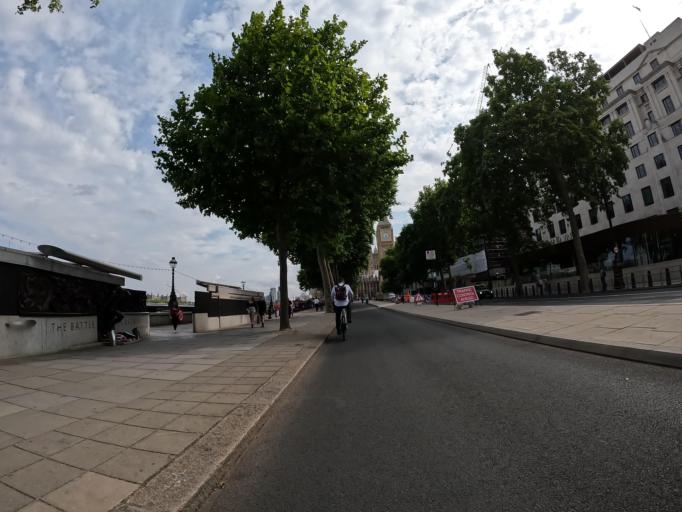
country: GB
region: England
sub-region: Greater London
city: Bromley
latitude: 51.3985
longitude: 0.0326
